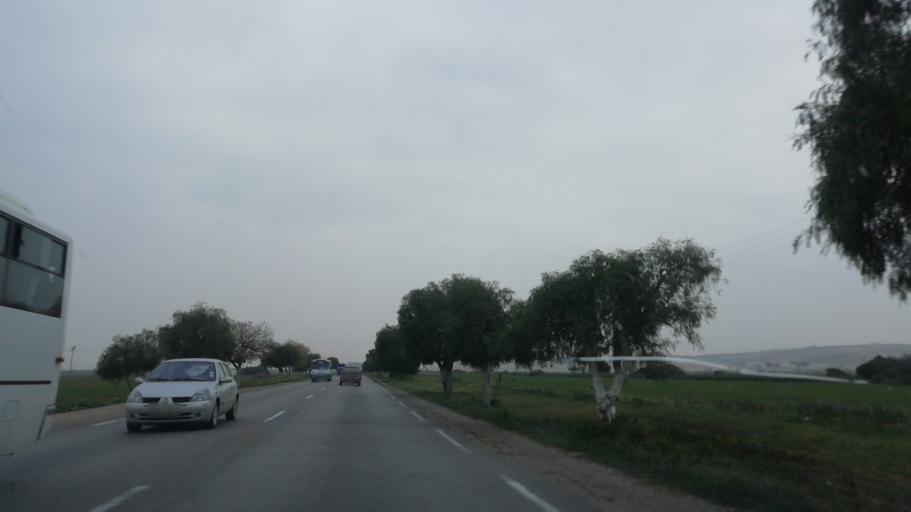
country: DZ
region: Mascara
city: Sig
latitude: 35.5480
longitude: -0.2908
